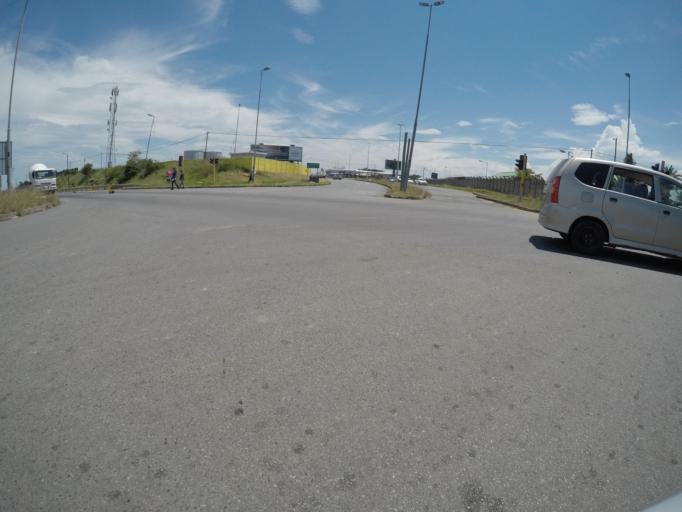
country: ZA
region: Eastern Cape
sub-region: Buffalo City Metropolitan Municipality
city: East London
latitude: -33.0383
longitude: 27.8326
